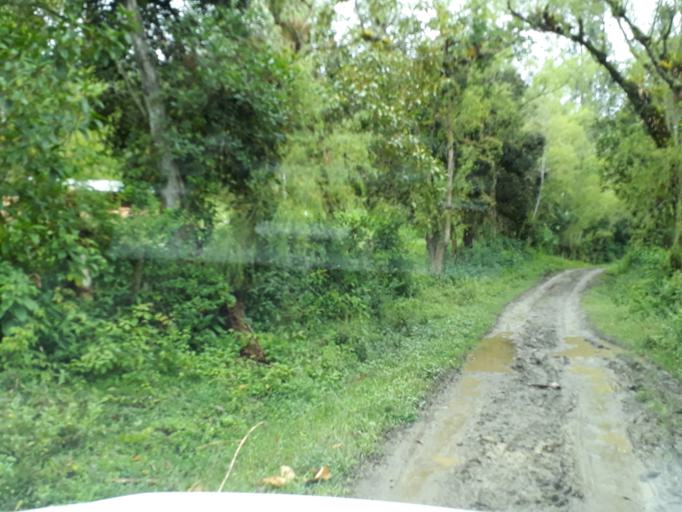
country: CO
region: Cundinamarca
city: Junin
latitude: 4.7735
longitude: -73.6422
